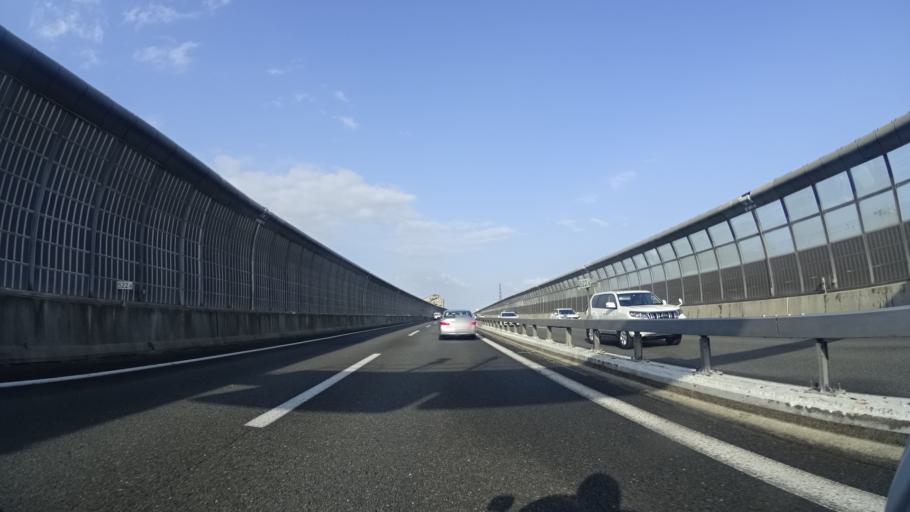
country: JP
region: Osaka
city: Suita
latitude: 34.7597
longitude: 135.4871
